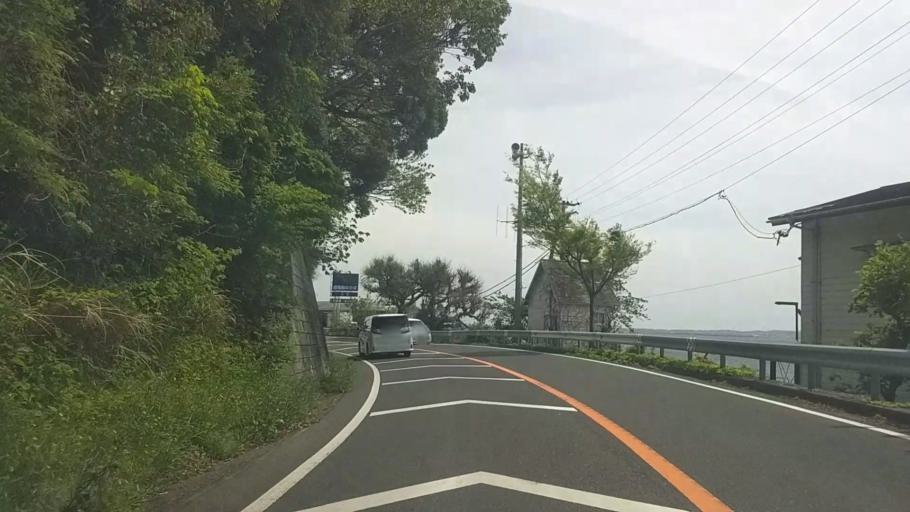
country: JP
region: Shizuoka
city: Kosai-shi
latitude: 34.7680
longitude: 137.5494
